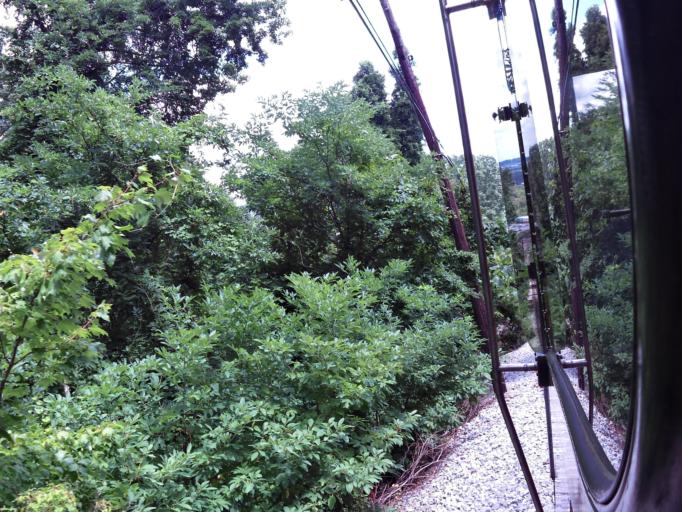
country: US
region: Tennessee
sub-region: Hamilton County
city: Lookout Mountain
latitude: 35.0083
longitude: -85.3341
